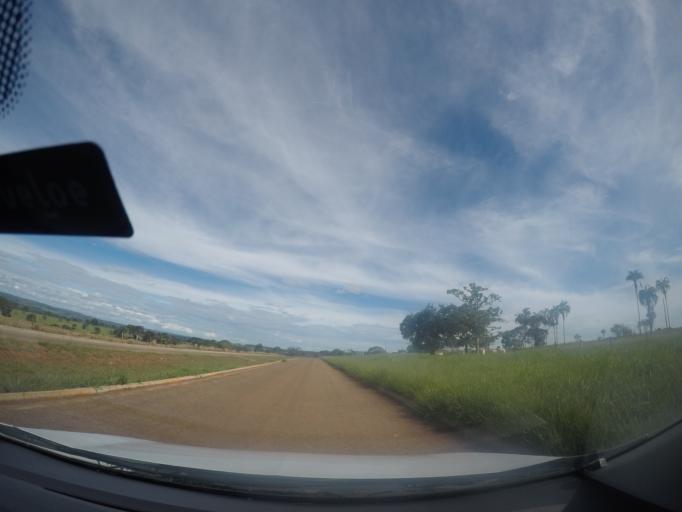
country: BR
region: Goias
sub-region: Inhumas
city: Inhumas
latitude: -16.4010
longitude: -49.4711
